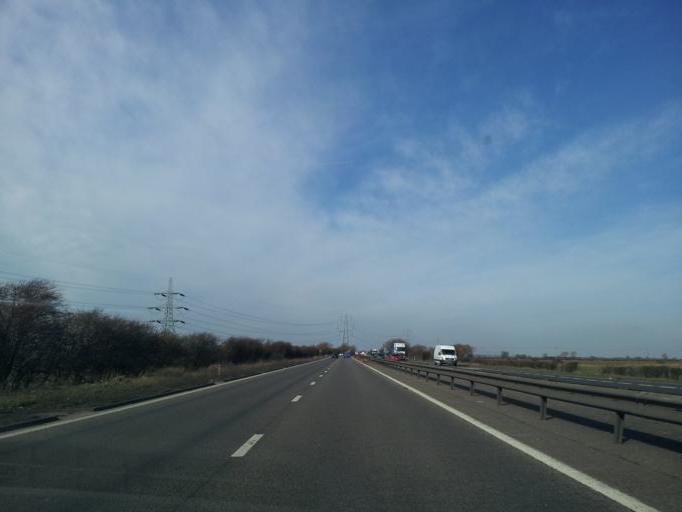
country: GB
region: England
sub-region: Lincolnshire
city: Long Bennington
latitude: 53.0073
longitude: -0.7635
